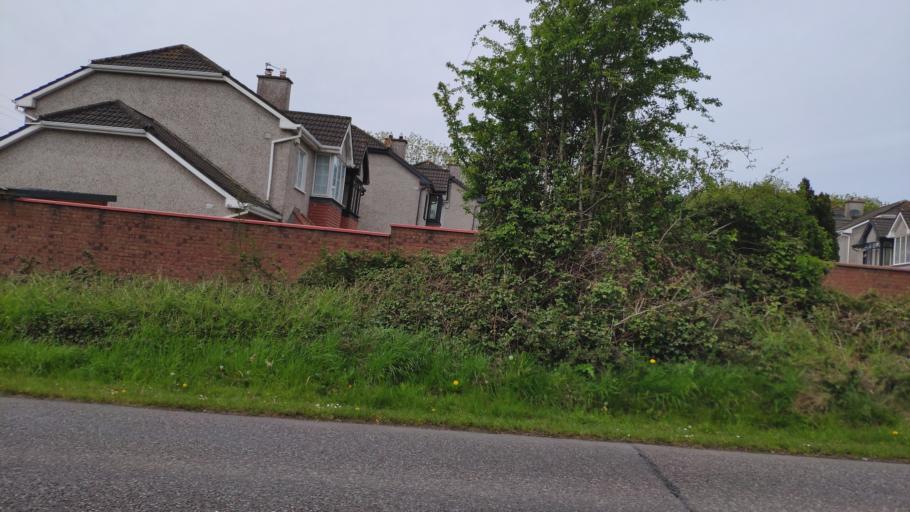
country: IE
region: Munster
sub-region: County Cork
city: Cork
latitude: 51.9240
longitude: -8.4560
